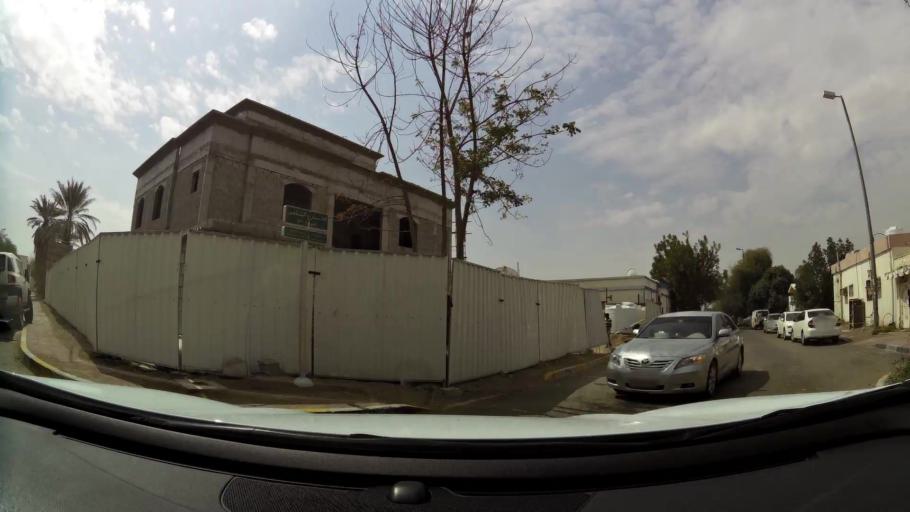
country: AE
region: Abu Dhabi
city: Al Ain
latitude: 24.2133
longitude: 55.7854
